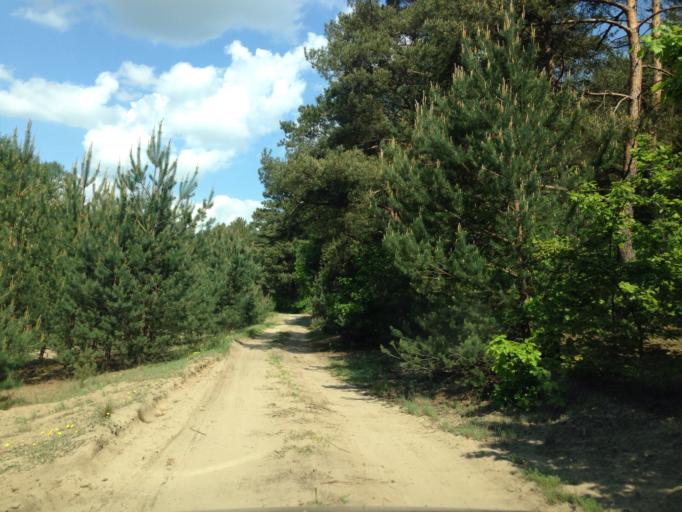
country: PL
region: Kujawsko-Pomorskie
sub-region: Powiat brodnicki
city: Brodnica
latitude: 53.3311
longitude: 19.3566
